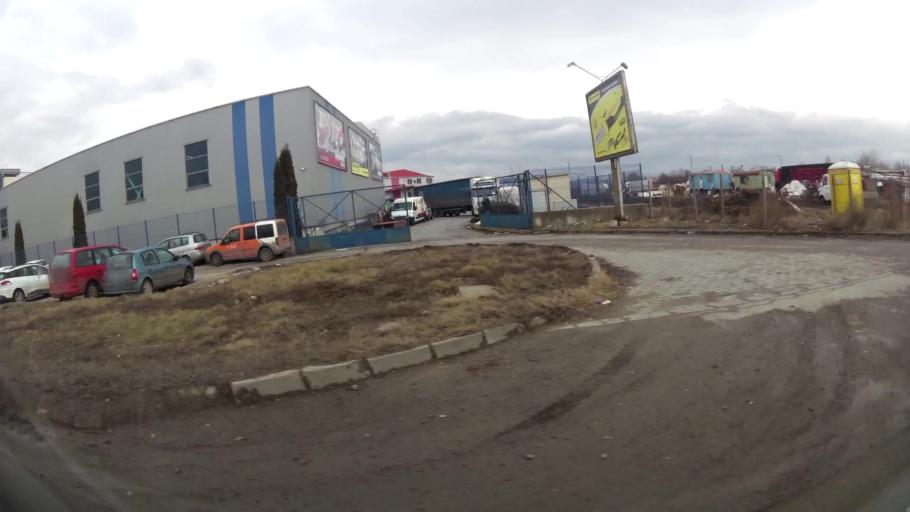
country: BG
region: Sofiya
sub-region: Obshtina Bozhurishte
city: Bozhurishte
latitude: 42.7547
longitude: 23.2722
